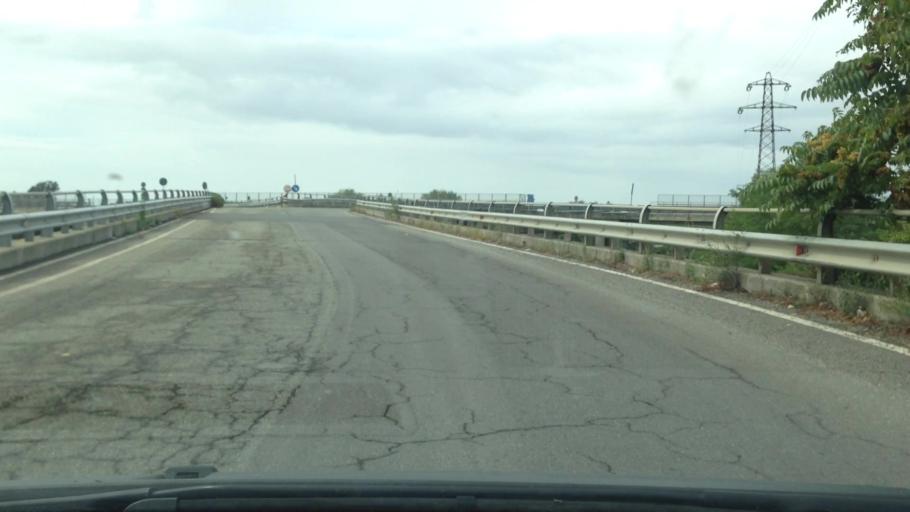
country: IT
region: Piedmont
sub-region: Provincia di Alessandria
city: Tortona
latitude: 44.8956
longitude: 8.8412
